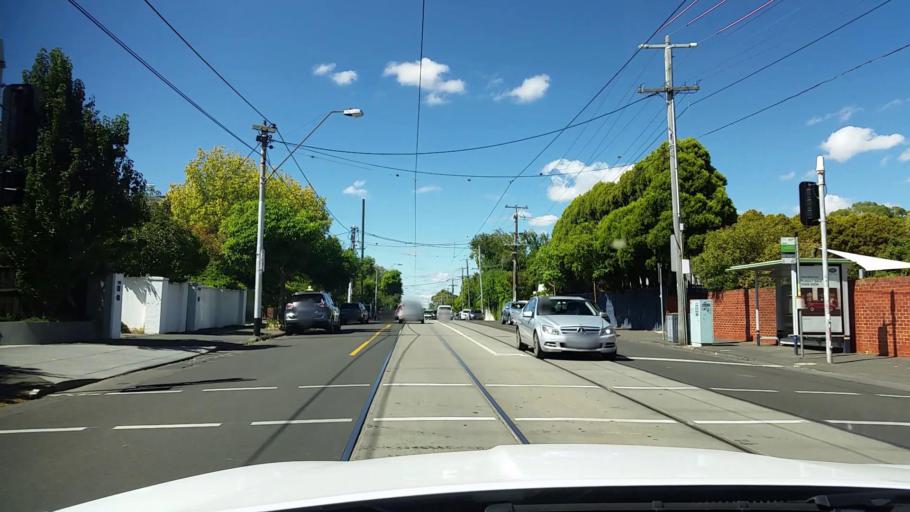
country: AU
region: Victoria
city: Toorak
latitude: -37.8511
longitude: 145.0262
